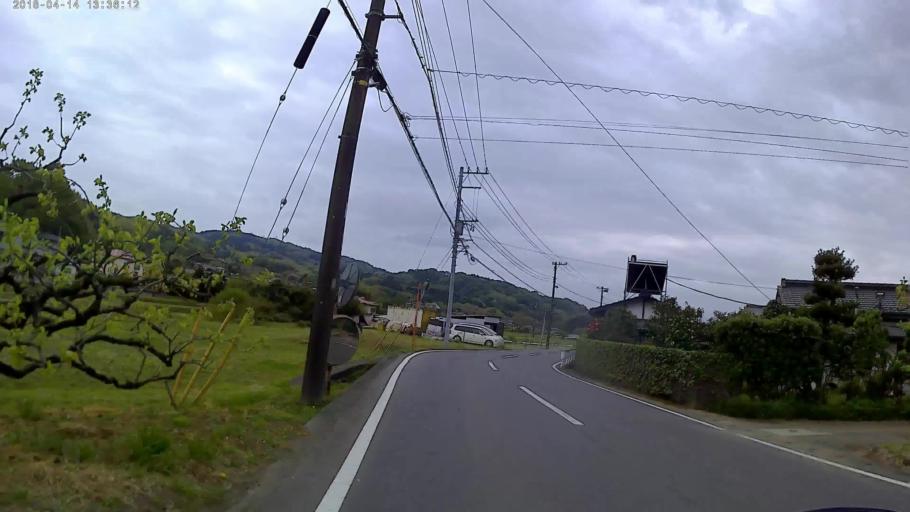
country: JP
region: Kanagawa
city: Hadano
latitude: 35.3313
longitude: 139.1639
